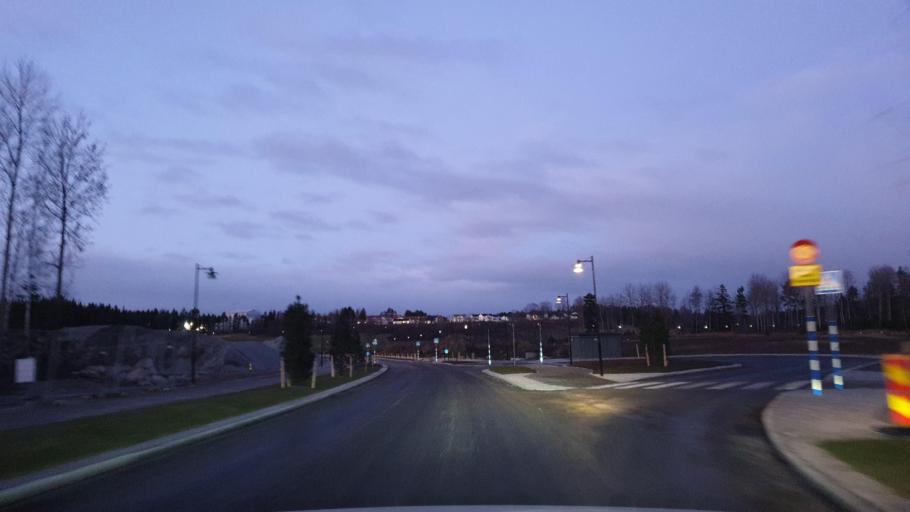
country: SE
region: Stockholm
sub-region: Sigtuna Kommun
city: Marsta
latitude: 59.6126
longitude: 17.7958
